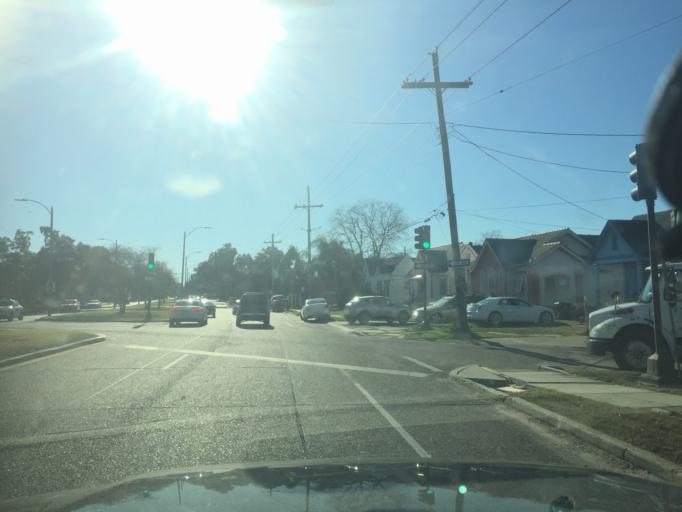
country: US
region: Louisiana
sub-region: Orleans Parish
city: New Orleans
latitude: 29.9878
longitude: -90.0678
